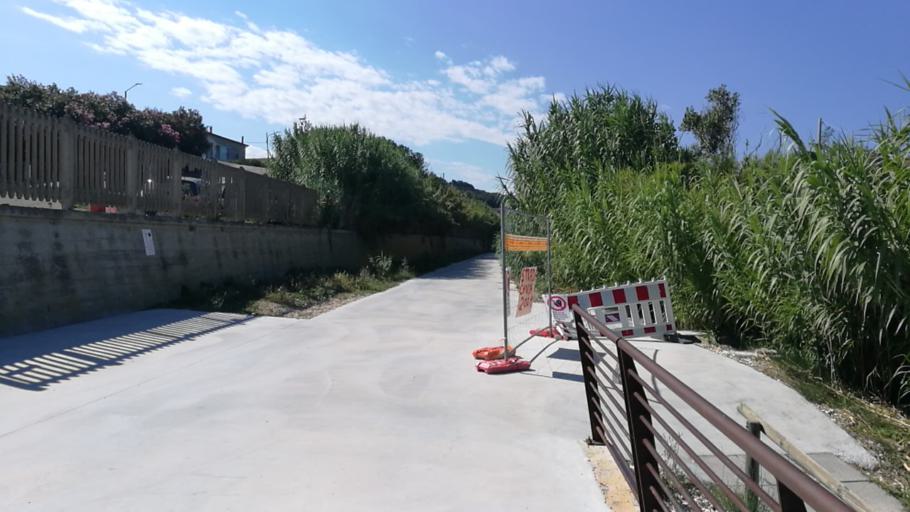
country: IT
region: Abruzzo
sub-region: Provincia di Chieti
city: Marina di San Vito
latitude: 42.2871
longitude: 14.4812
